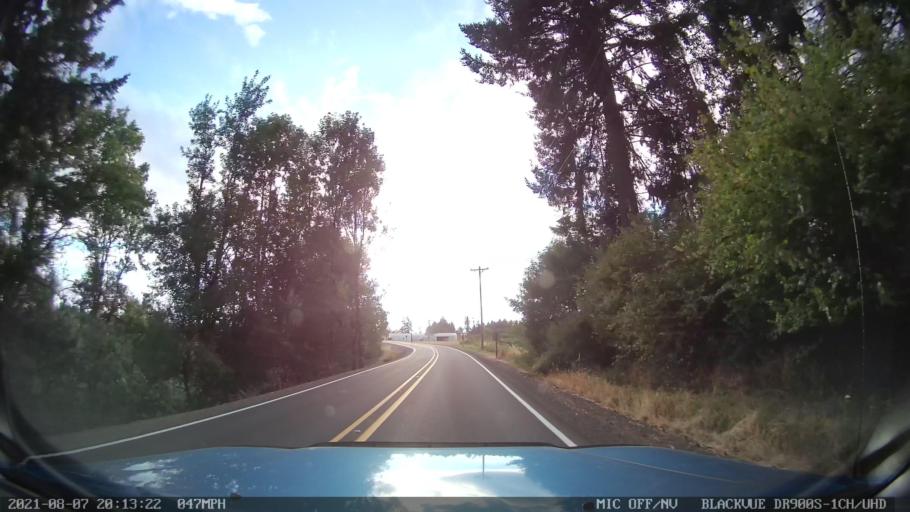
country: US
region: Oregon
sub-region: Marion County
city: Hayesville
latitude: 44.9568
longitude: -122.9227
